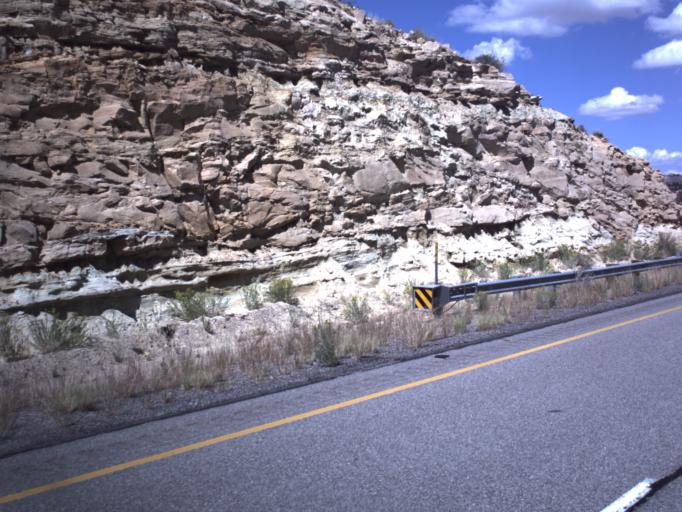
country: US
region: Utah
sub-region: Emery County
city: Ferron
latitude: 38.8568
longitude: -110.8690
